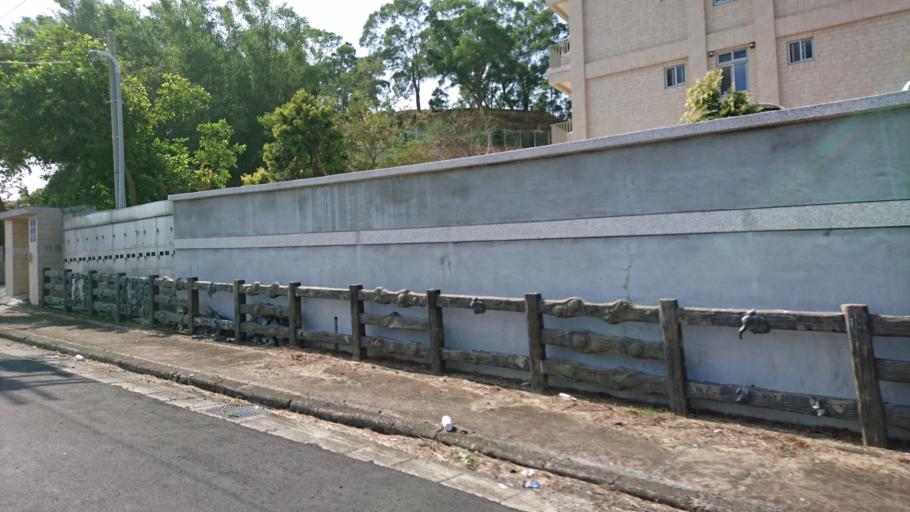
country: TW
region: Taiwan
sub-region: Hsinchu
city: Hsinchu
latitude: 24.7184
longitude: 120.9238
